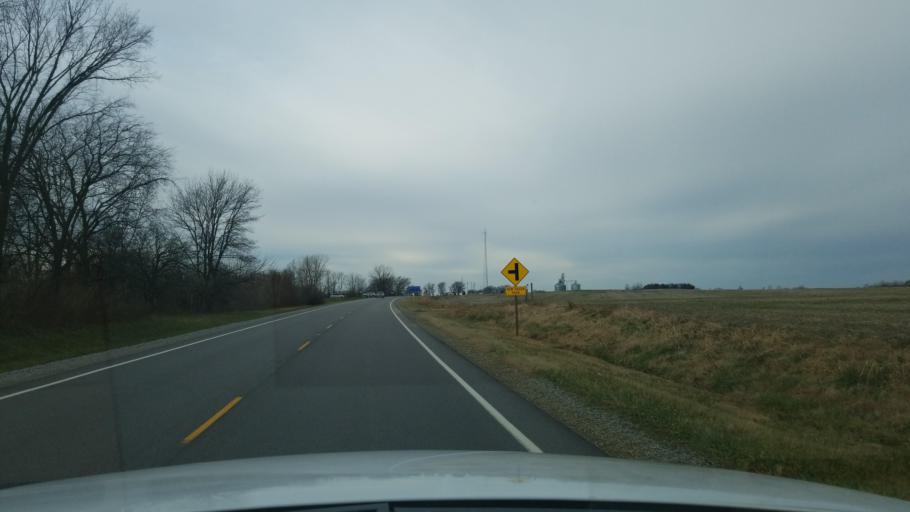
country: US
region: Illinois
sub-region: White County
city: Carmi
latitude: 37.9090
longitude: -88.1365
